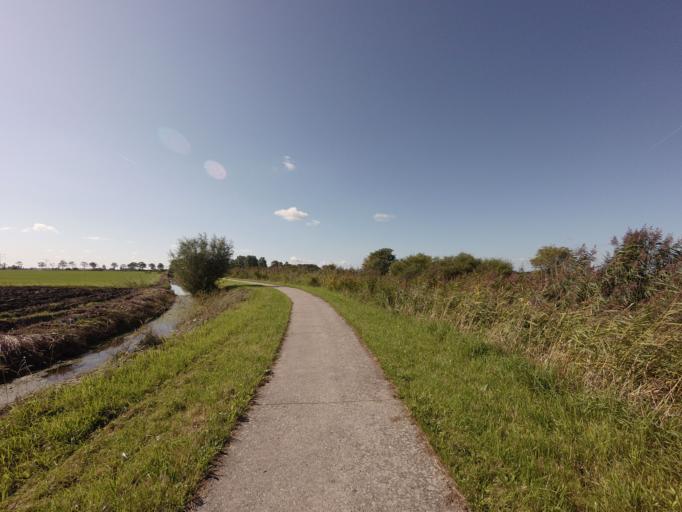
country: NL
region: Friesland
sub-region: Gemeente Leeuwarden
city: Wirdum
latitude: 53.1529
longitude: 5.7646
